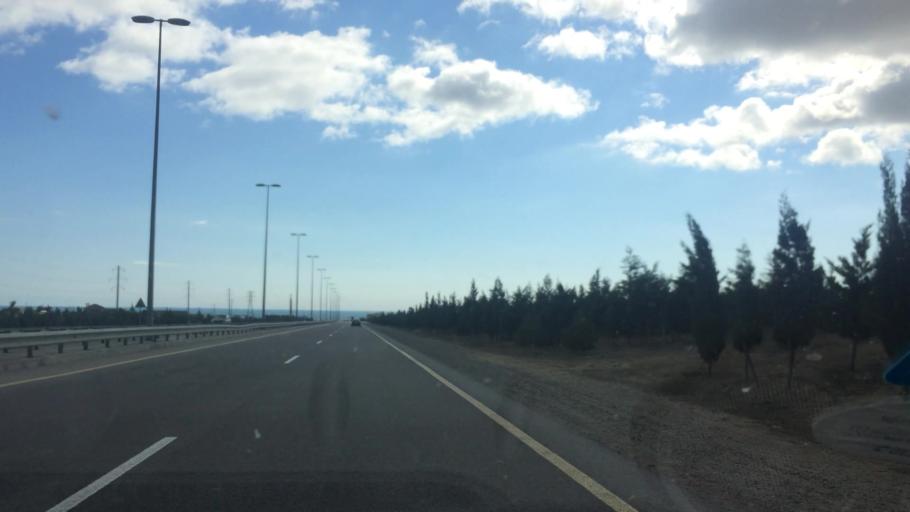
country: AZ
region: Baki
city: Zyrya
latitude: 40.4037
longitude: 50.3050
